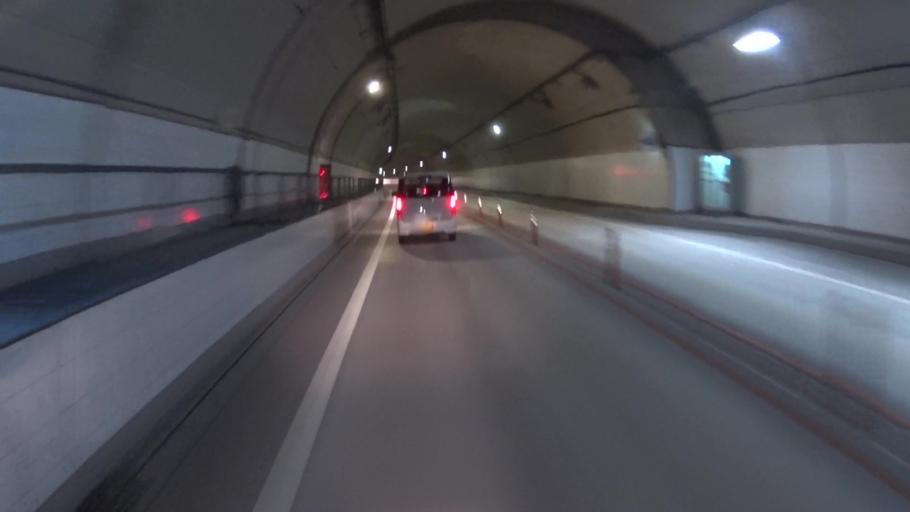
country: JP
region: Kyoto
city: Miyazu
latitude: 35.5288
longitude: 135.1727
